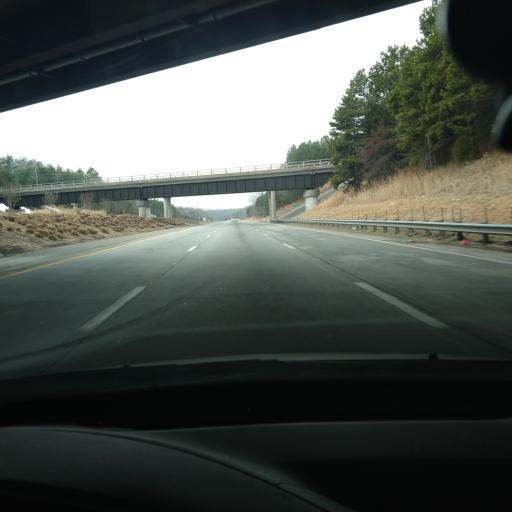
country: US
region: North Carolina
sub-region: Davidson County
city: Welcome
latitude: 35.8734
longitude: -80.2480
